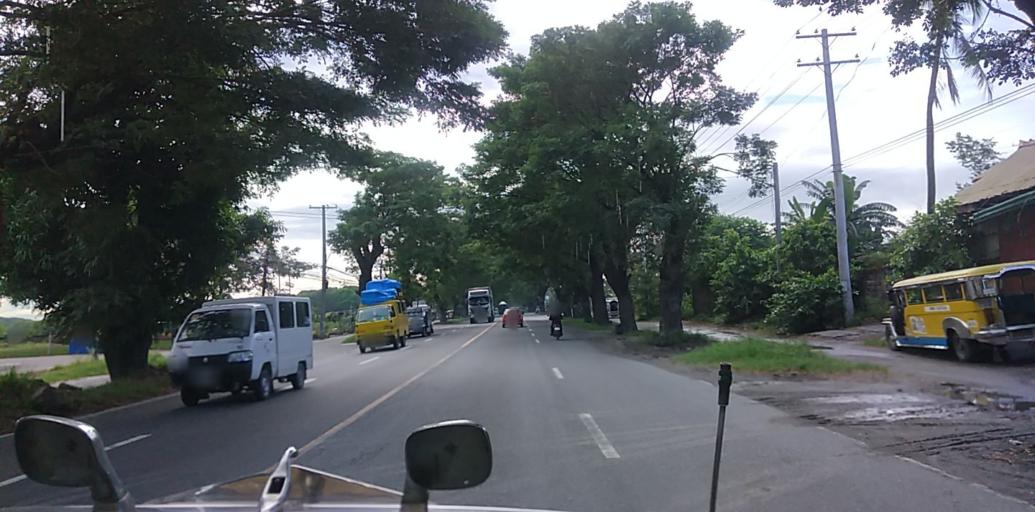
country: PH
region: Central Luzon
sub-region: Province of Pampanga
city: Telabastagan
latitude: 15.1089
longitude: 120.6135
